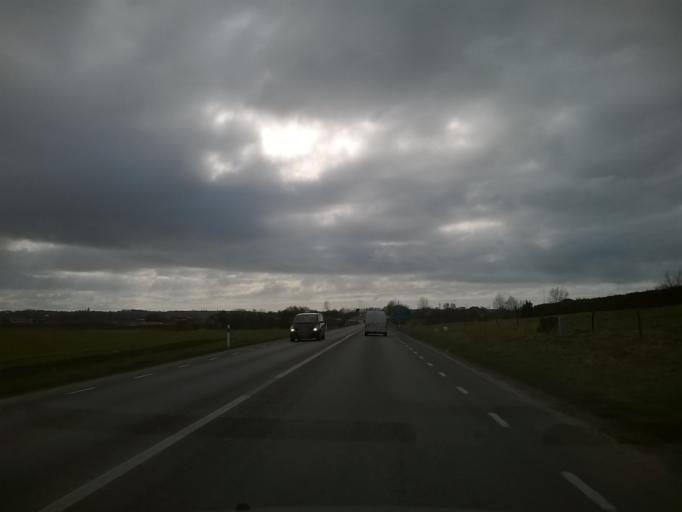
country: SE
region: Halland
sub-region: Varbergs Kommun
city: Varberg
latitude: 57.1315
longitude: 12.3188
